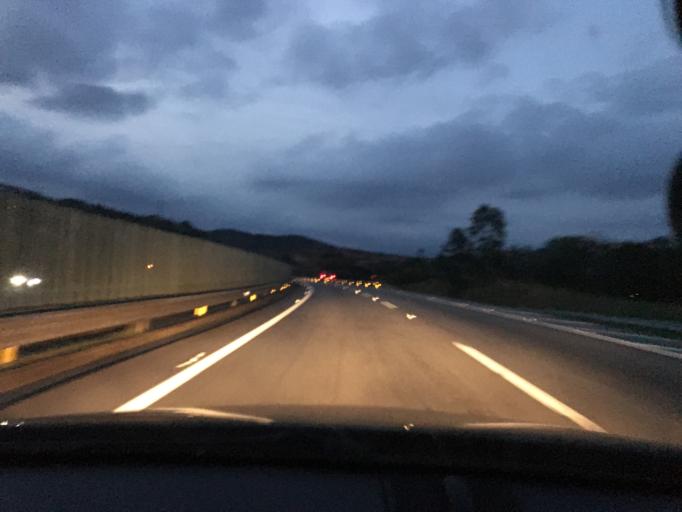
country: BR
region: Sao Paulo
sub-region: Santa Isabel
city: Santa Isabel
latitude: -23.3413
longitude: -46.1275
